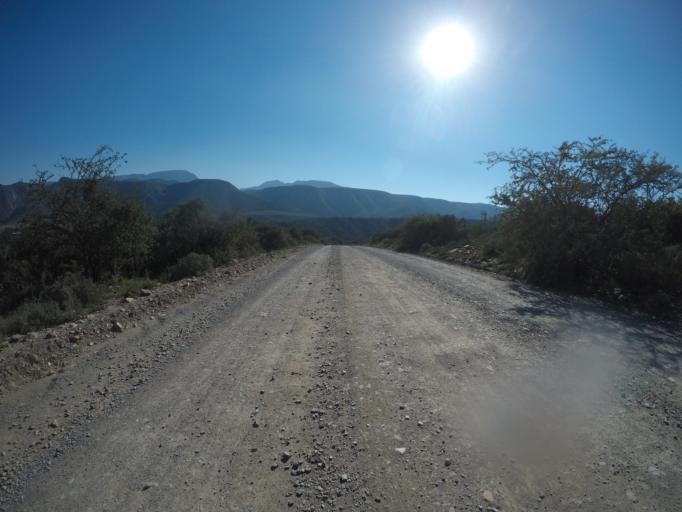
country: ZA
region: Eastern Cape
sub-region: Cacadu District Municipality
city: Kruisfontein
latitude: -33.6711
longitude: 24.5770
